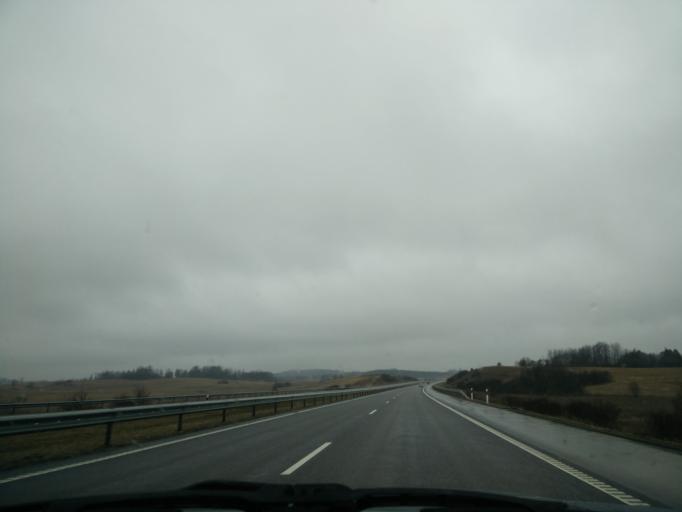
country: LT
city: Skaudvile
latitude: 55.4922
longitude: 22.5245
